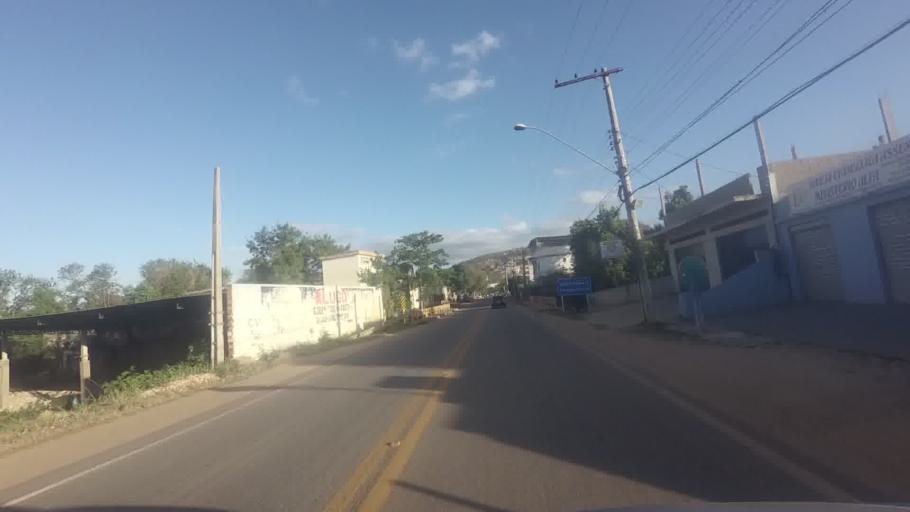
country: BR
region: Espirito Santo
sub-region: Cachoeiro De Itapemirim
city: Cachoeiro de Itapemirim
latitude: -20.8297
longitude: -41.1793
